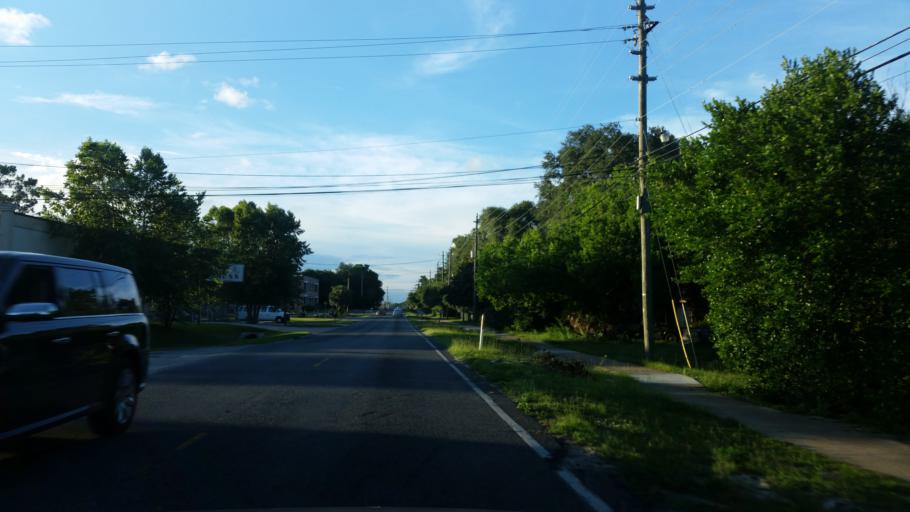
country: US
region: Florida
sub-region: Escambia County
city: Warrington
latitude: 30.3995
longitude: -87.2737
